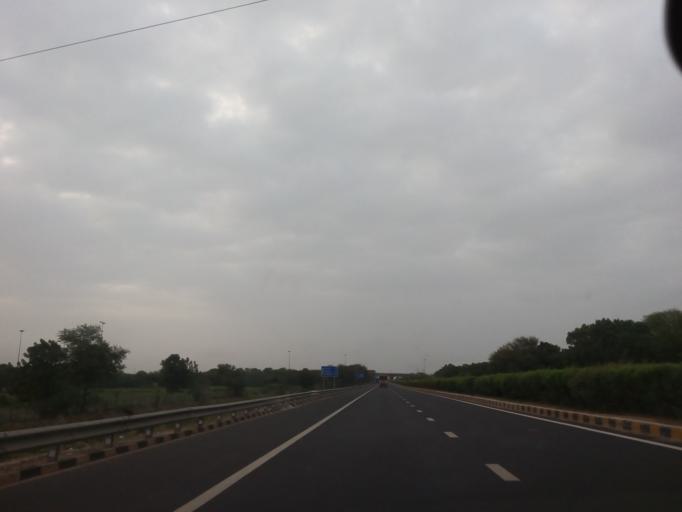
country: IN
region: Gujarat
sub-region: Ahmadabad
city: Ahmedabad
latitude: 22.9726
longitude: 72.6560
